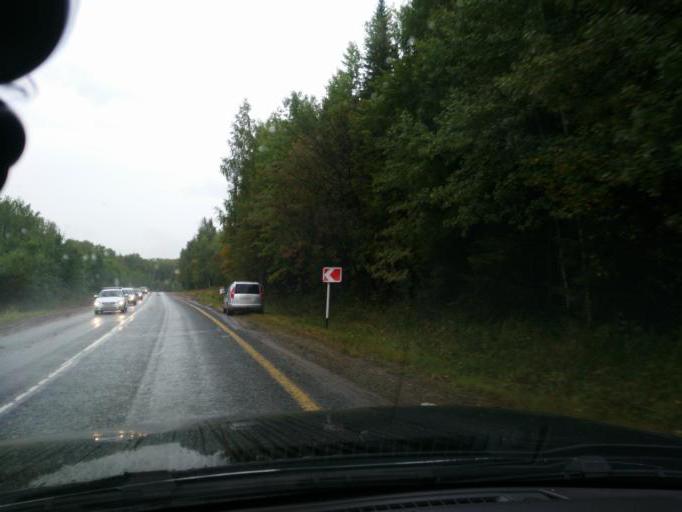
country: RU
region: Perm
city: Yugo-Kamskiy
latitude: 57.5162
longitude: 55.6875
